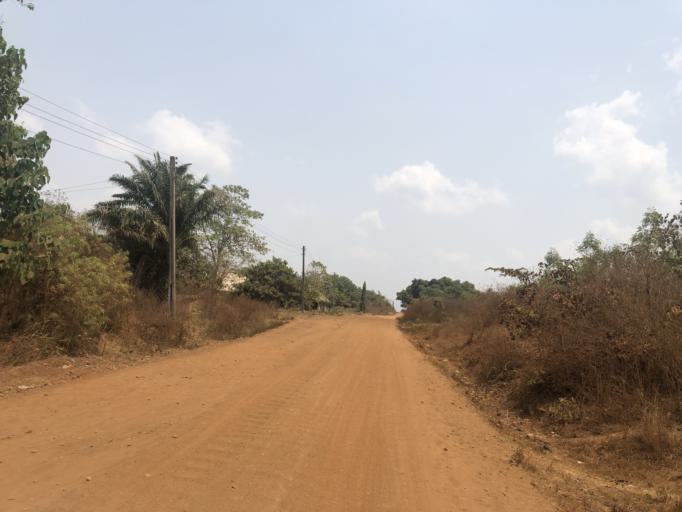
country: NG
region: Osun
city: Bode Osi
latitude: 7.8008
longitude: 4.1490
